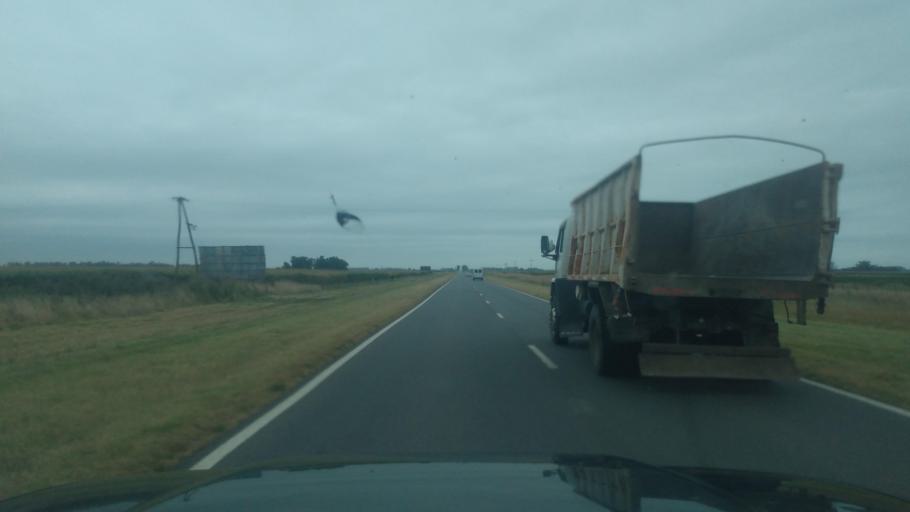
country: AR
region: Buenos Aires
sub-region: Partido de Nueve de Julio
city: Nueve de Julio
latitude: -35.3868
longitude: -60.7334
